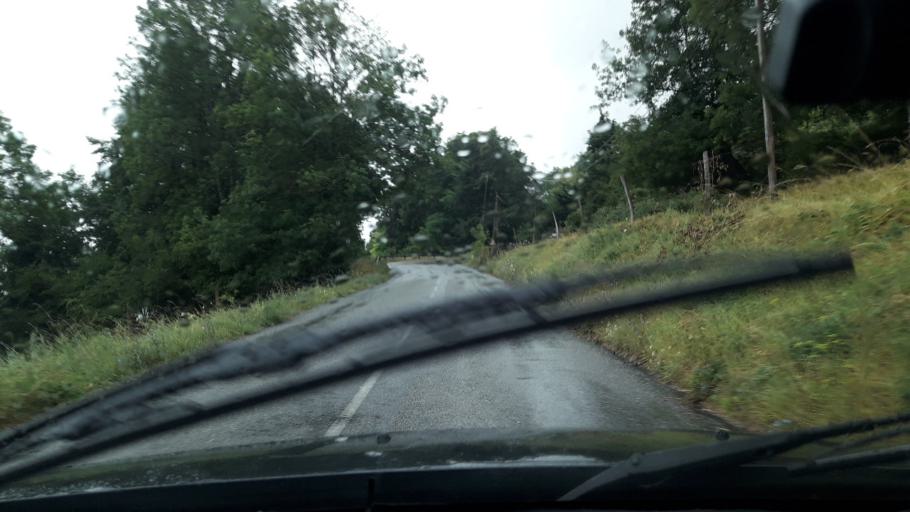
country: FR
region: Rhone-Alpes
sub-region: Departement de la Savoie
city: Saint-Baldoph
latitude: 45.5337
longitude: 5.9464
